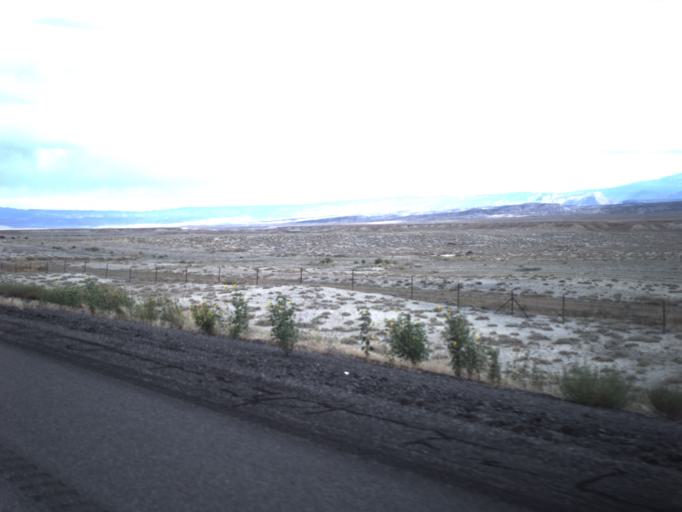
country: US
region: Utah
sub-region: Grand County
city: Moab
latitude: 38.9329
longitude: -109.4451
